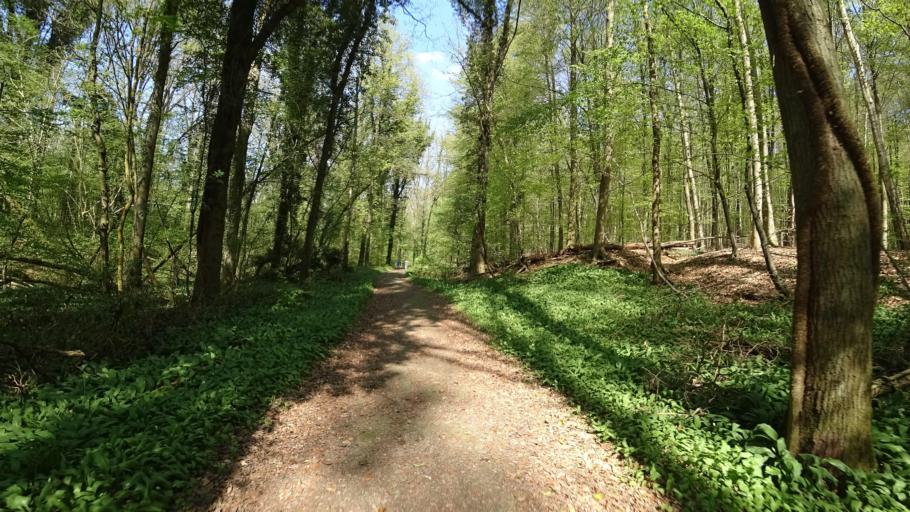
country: BE
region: Wallonia
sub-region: Province du Brabant Wallon
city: Braine-le-Chateau
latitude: 50.7127
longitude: 4.2779
